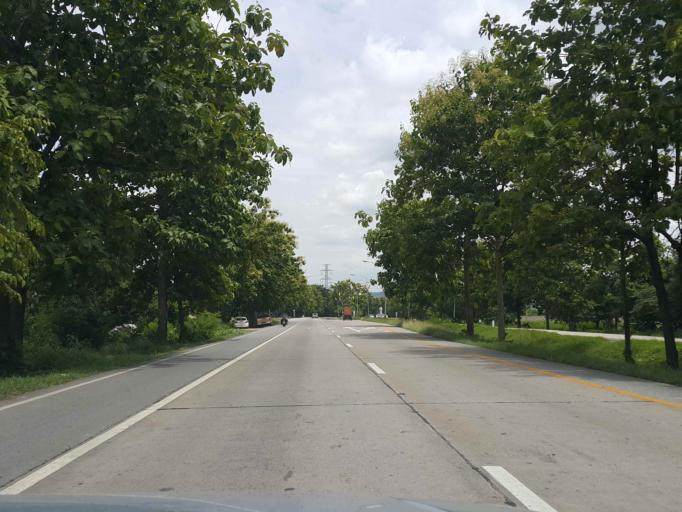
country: TH
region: Lamphun
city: Lamphun
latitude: 18.5391
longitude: 99.0703
